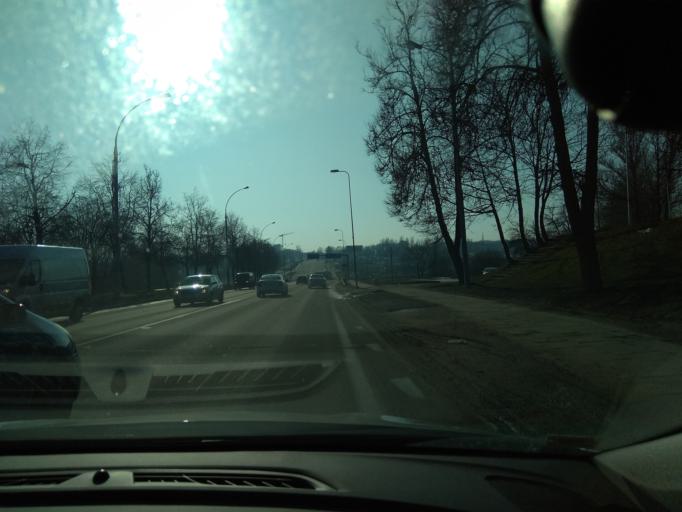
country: LT
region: Vilnius County
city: Naujamiestis
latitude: 54.6597
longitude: 25.2729
